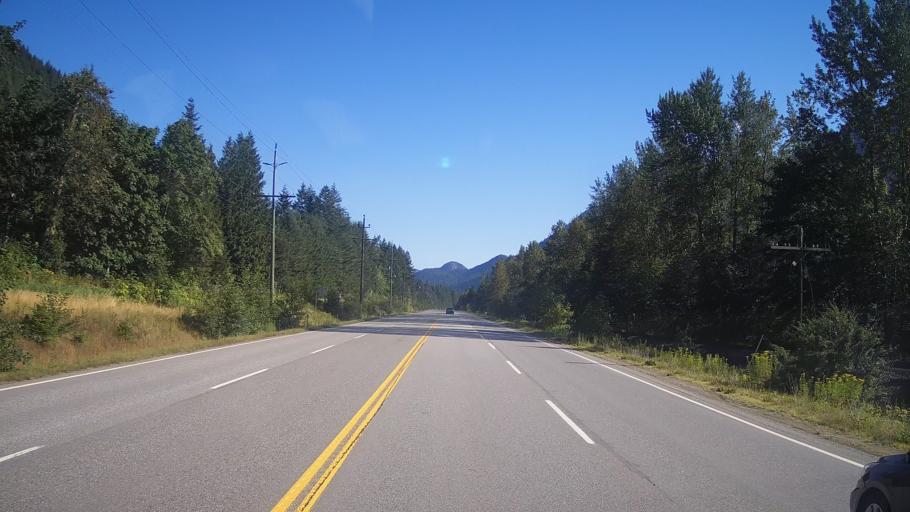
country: CA
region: British Columbia
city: Hope
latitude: 49.4923
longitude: -121.4207
